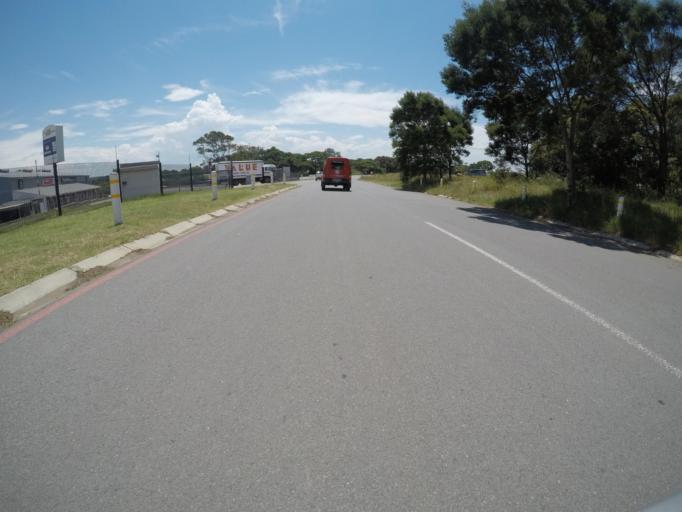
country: ZA
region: Eastern Cape
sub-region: Buffalo City Metropolitan Municipality
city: East London
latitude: -33.0362
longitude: 27.8412
